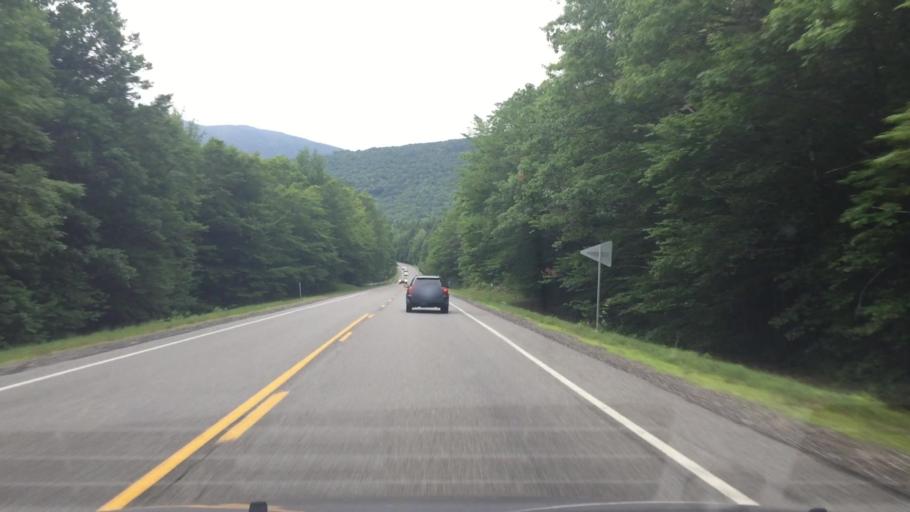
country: US
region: New Hampshire
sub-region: Carroll County
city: North Conway
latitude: 44.0935
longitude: -71.3544
